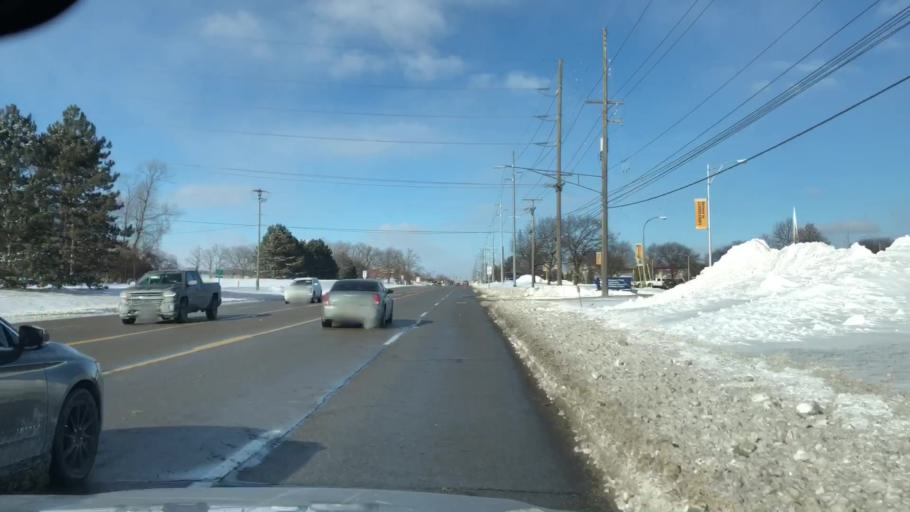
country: US
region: Michigan
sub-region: Wayne County
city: Northville
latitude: 42.4172
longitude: -83.4326
